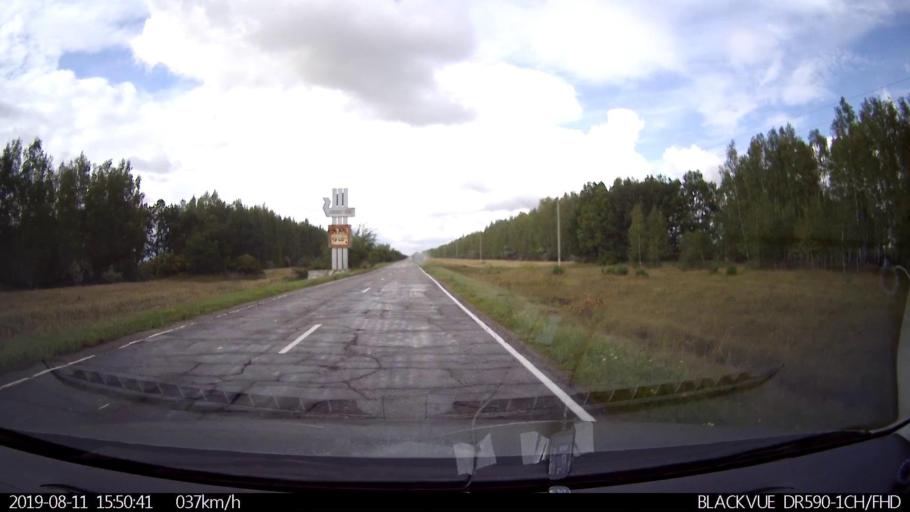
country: RU
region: Ulyanovsk
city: Ignatovka
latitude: 53.9135
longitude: 47.6559
